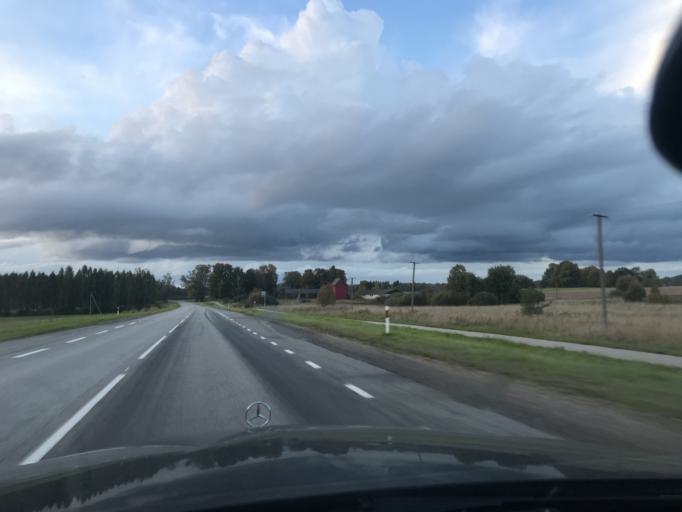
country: EE
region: Vorumaa
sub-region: Antsla vald
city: Vana-Antsla
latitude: 57.9364
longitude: 26.3126
